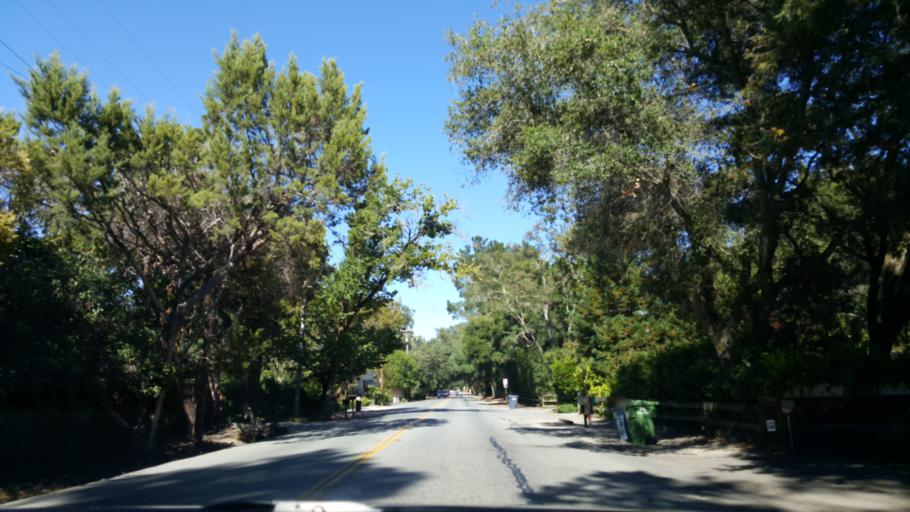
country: US
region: California
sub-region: San Mateo County
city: Woodside
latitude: 37.4264
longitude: -122.2649
